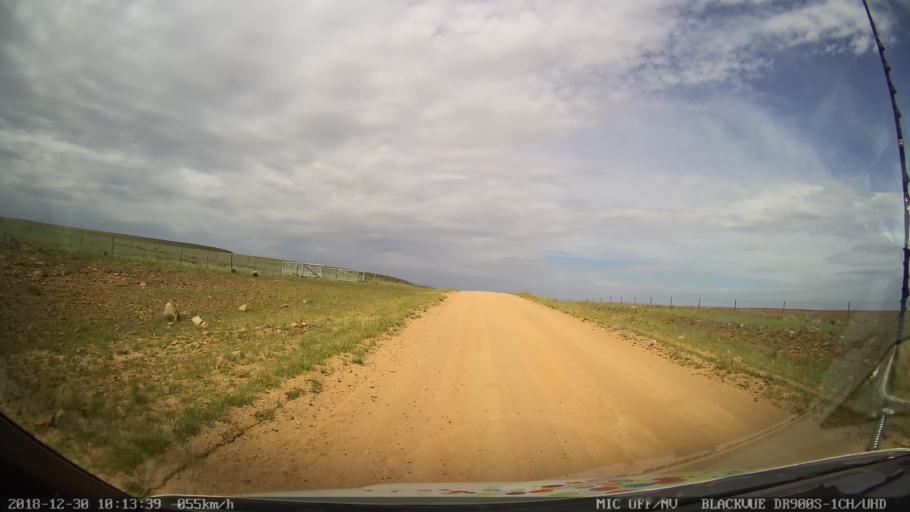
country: AU
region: New South Wales
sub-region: Snowy River
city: Berridale
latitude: -36.5389
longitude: 149.0631
